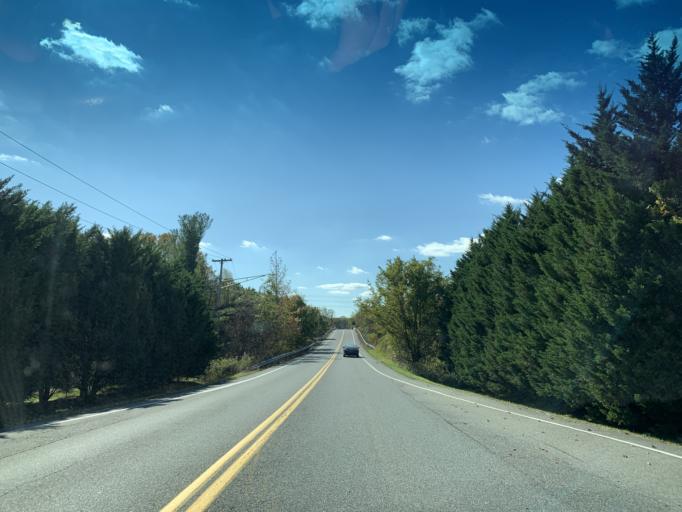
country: US
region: Maryland
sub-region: Anne Arundel County
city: Gambrills
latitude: 39.0776
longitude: -76.6605
